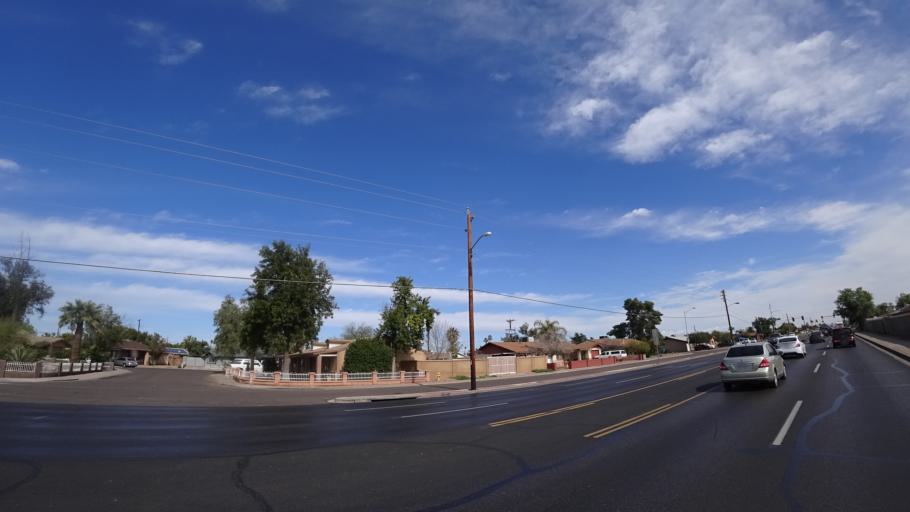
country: US
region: Arizona
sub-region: Maricopa County
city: Glendale
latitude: 33.4805
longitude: -112.1799
